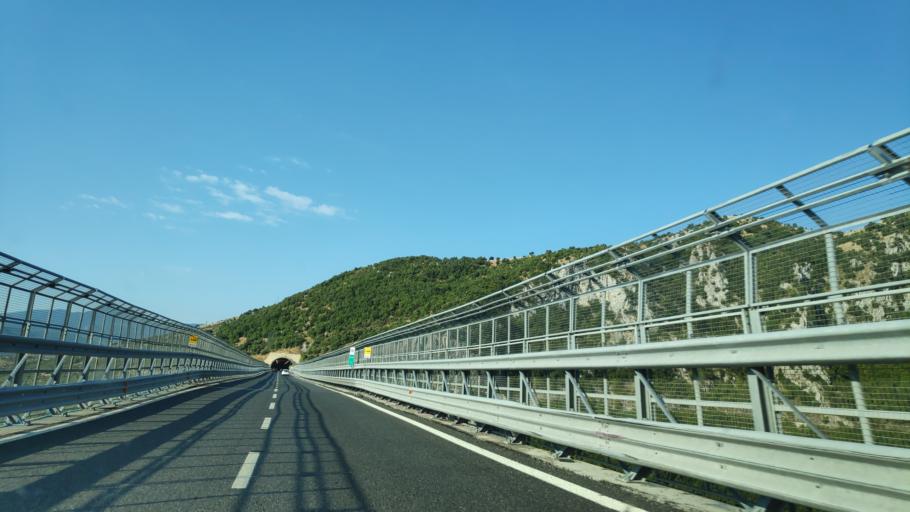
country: IT
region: Calabria
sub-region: Provincia di Cosenza
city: Morano Calabro
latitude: 39.8802
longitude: 16.1295
